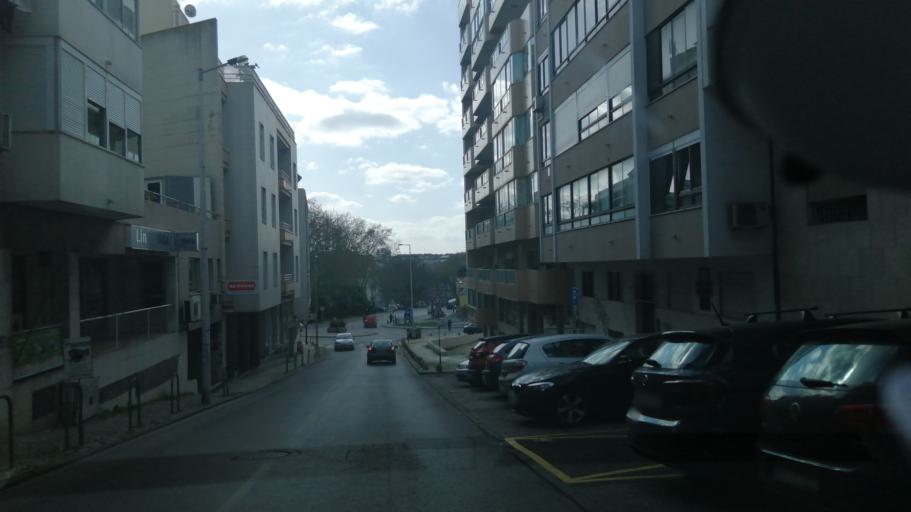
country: PT
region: Setubal
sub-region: Almada
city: Almada
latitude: 38.6754
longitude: -9.1626
